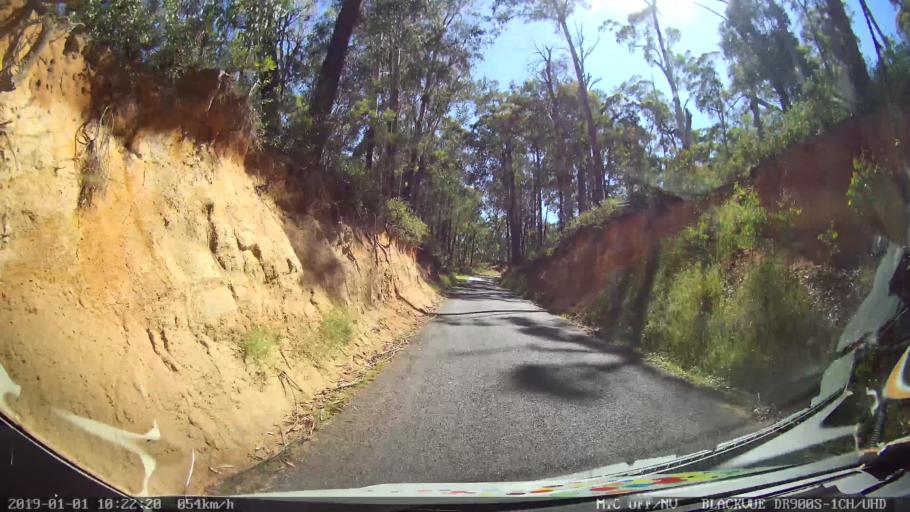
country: AU
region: New South Wales
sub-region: Snowy River
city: Jindabyne
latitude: -36.0783
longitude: 148.2029
